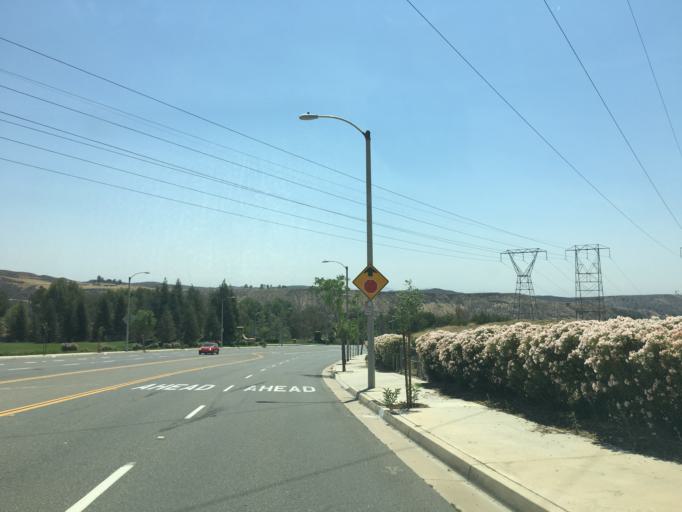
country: US
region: California
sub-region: Los Angeles County
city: Castaic
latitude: 34.5030
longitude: -118.6182
